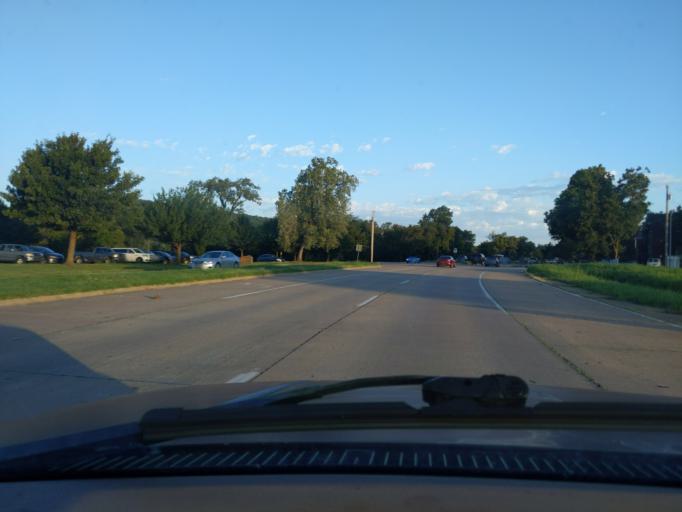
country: US
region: Oklahoma
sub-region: Tulsa County
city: Jenks
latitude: 36.0640
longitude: -95.9785
